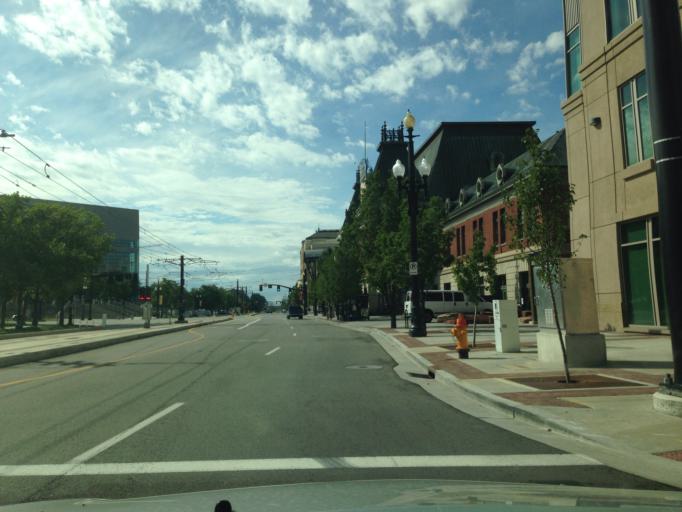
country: US
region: Utah
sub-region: Salt Lake County
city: Salt Lake City
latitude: 40.7703
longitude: -111.9026
